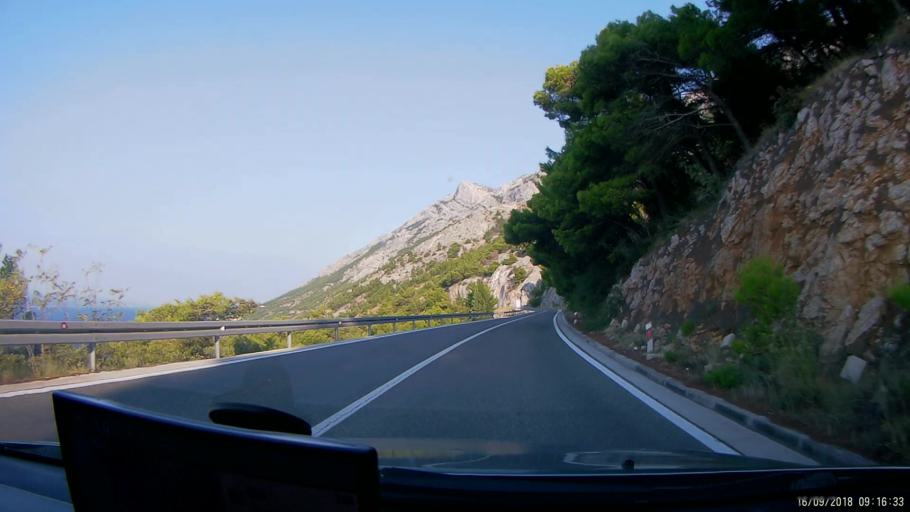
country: HR
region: Splitsko-Dalmatinska
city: Donja Brela
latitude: 43.4008
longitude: 16.8660
